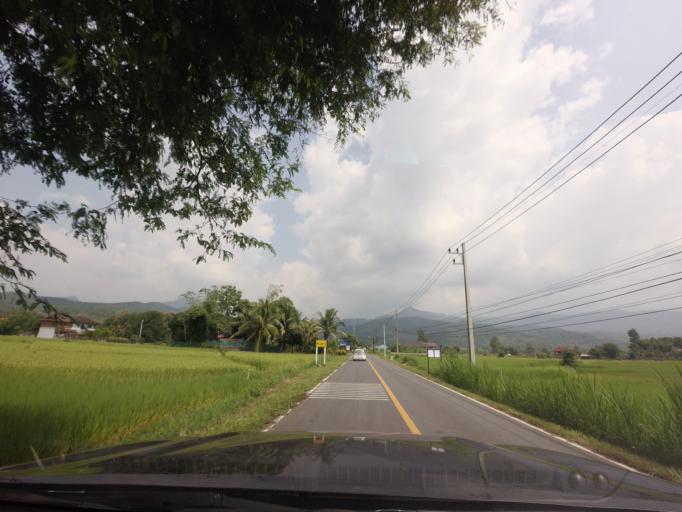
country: TH
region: Nan
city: Pua
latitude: 19.1745
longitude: 100.9407
